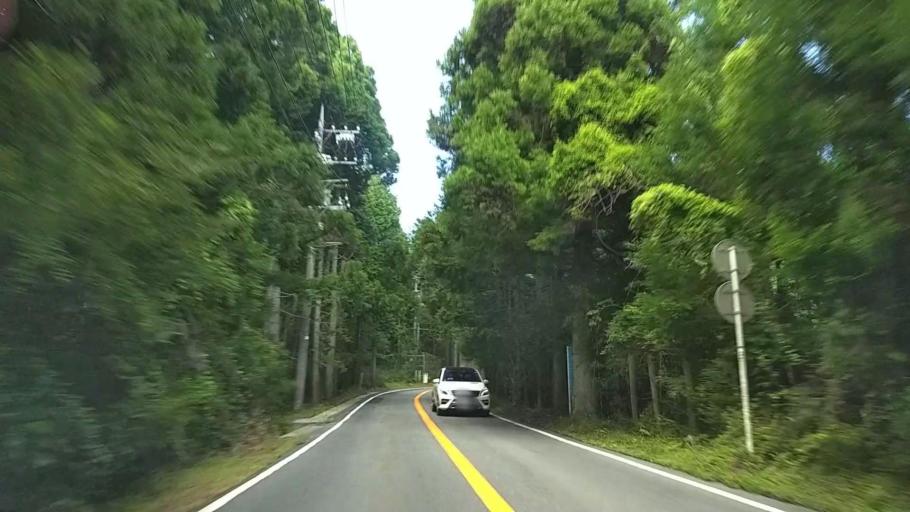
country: JP
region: Shizuoka
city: Gotemba
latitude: 35.2517
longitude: 138.8358
